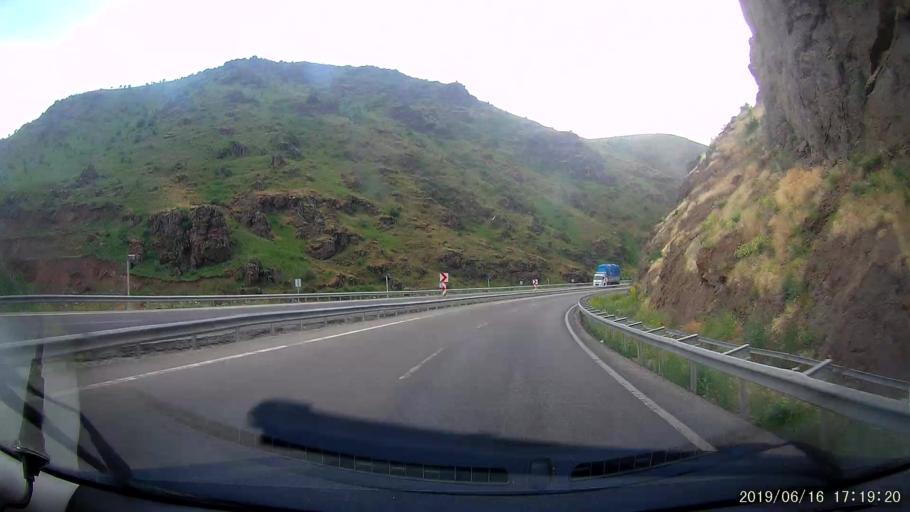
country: TR
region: Erzincan
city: Tercan
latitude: 39.8015
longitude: 40.5307
